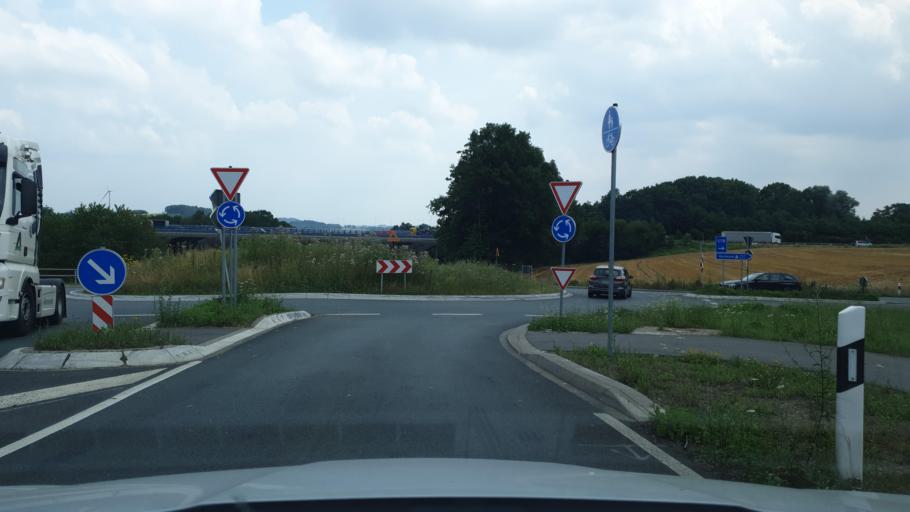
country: DE
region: North Rhine-Westphalia
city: Bad Oeynhausen
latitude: 52.1450
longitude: 8.7813
